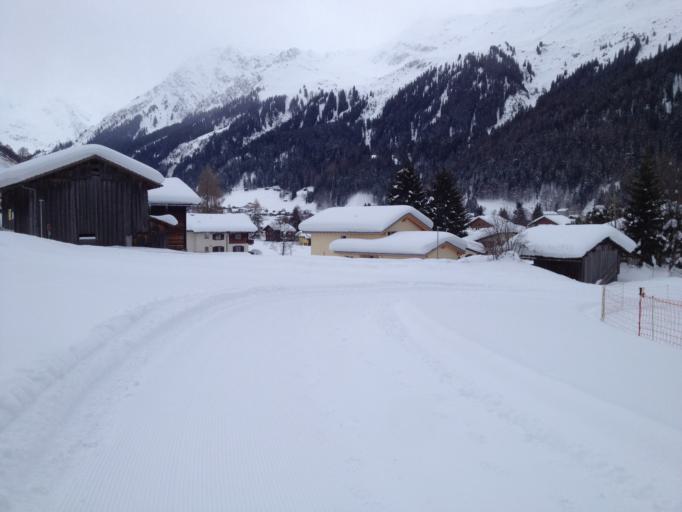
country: CH
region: Grisons
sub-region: Praettigau/Davos District
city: Klosters Serneus
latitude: 46.8679
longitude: 9.8913
